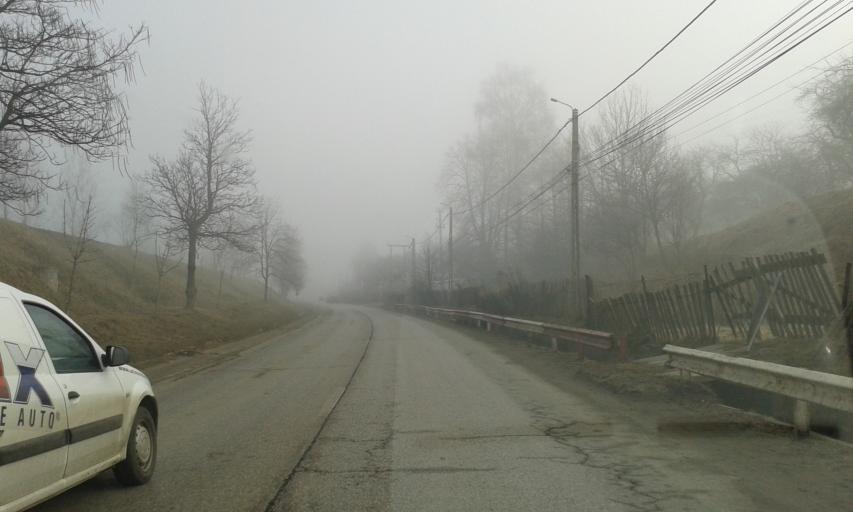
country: RO
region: Hunedoara
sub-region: Municipiul  Vulcan
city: Jiu-Paroseni
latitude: 45.3664
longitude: 23.2698
